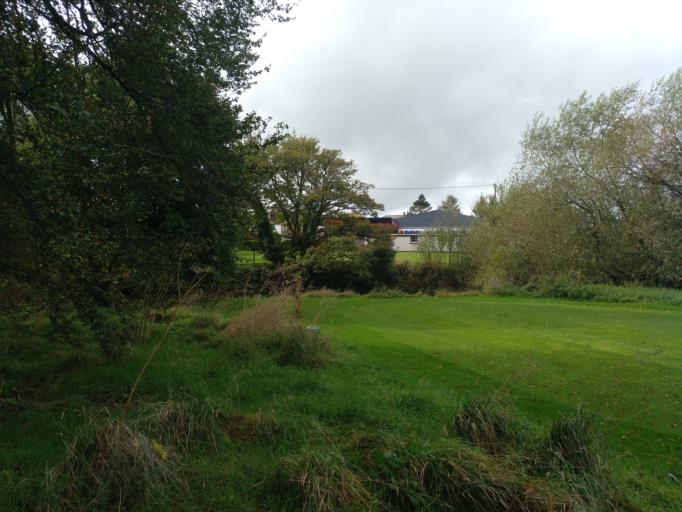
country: IE
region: Leinster
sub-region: Kilkenny
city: Castlecomer
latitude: 52.8002
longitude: -7.2088
